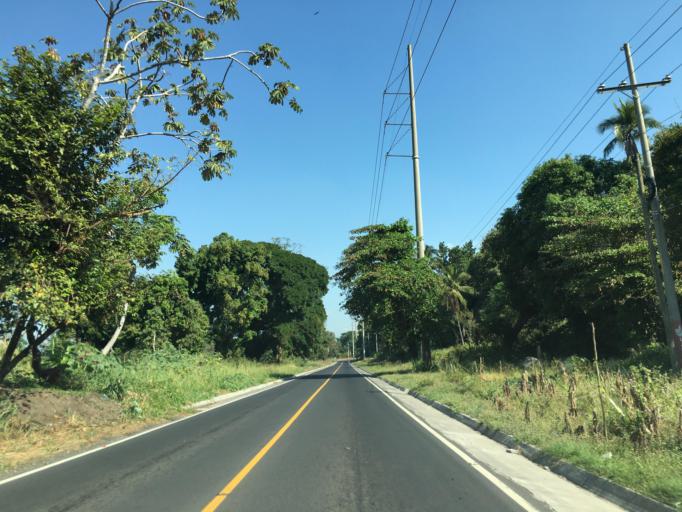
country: GT
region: Escuintla
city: Siquinala
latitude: 14.2834
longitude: -90.9688
